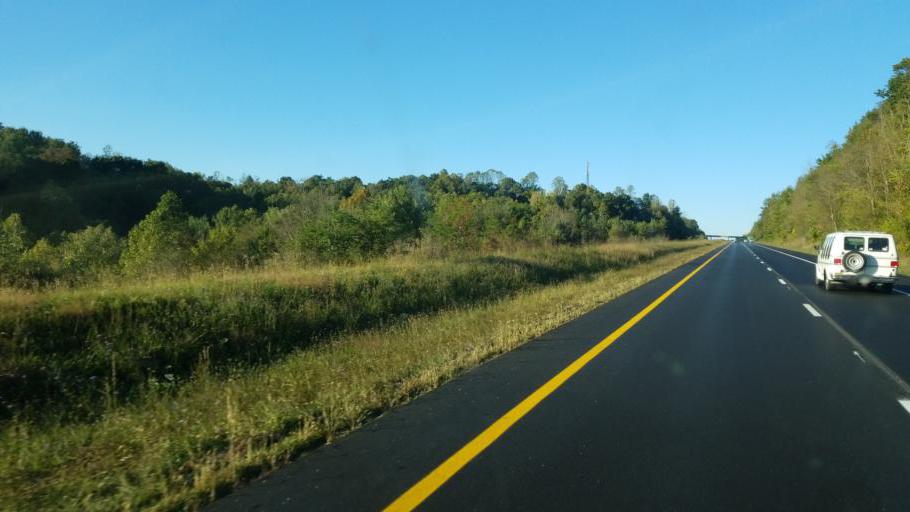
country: US
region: Ohio
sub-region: Guernsey County
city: Cambridge
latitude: 40.1181
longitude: -81.5577
